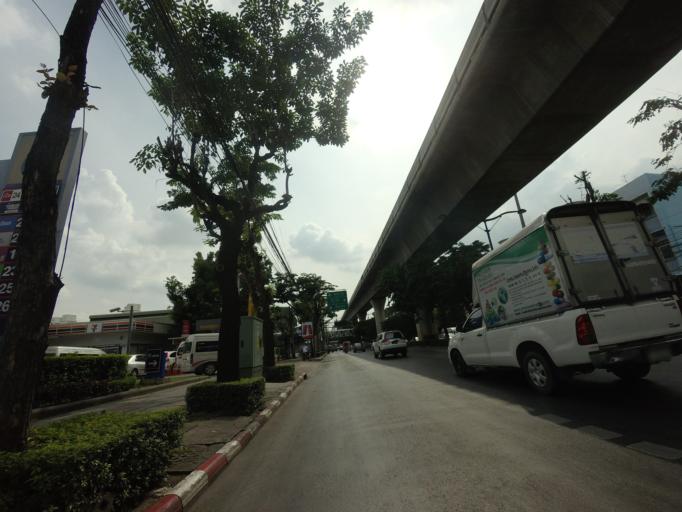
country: TH
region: Bangkok
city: Phaya Thai
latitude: 13.7688
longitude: 100.5406
